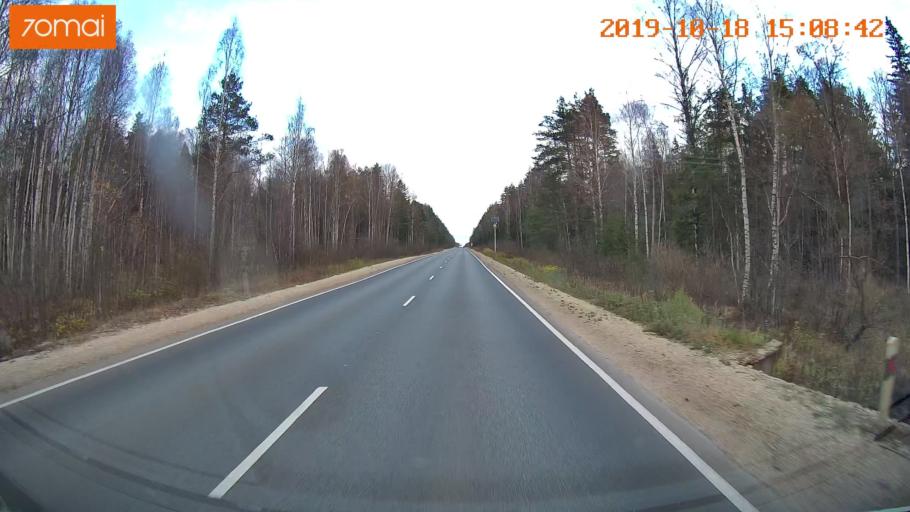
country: RU
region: Vladimir
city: Gus'-Khrustal'nyy
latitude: 55.5558
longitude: 40.6132
